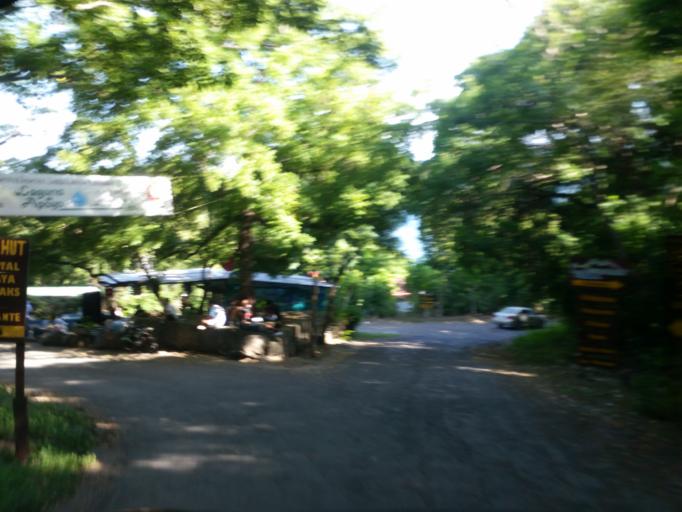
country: NI
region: Masaya
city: Catarina
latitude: 11.9299
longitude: -86.0558
